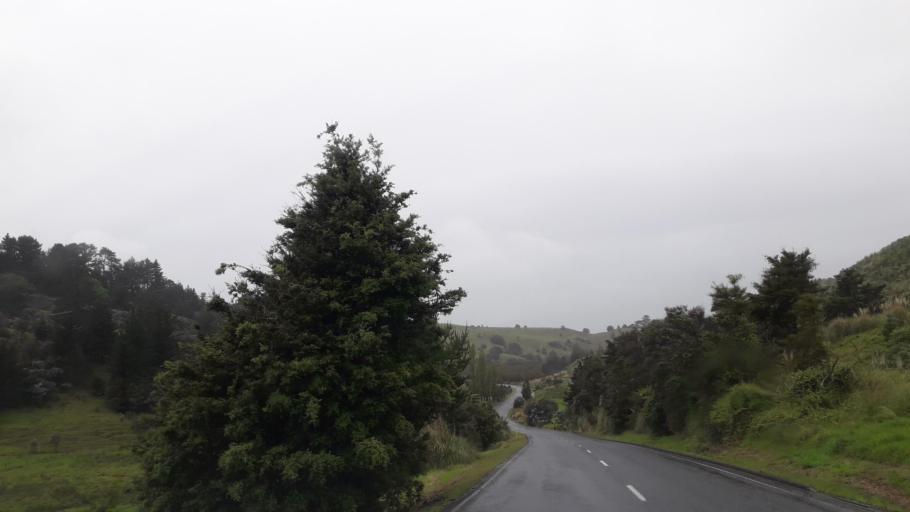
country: NZ
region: Northland
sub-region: Far North District
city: Kaitaia
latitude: -35.3584
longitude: 173.4676
